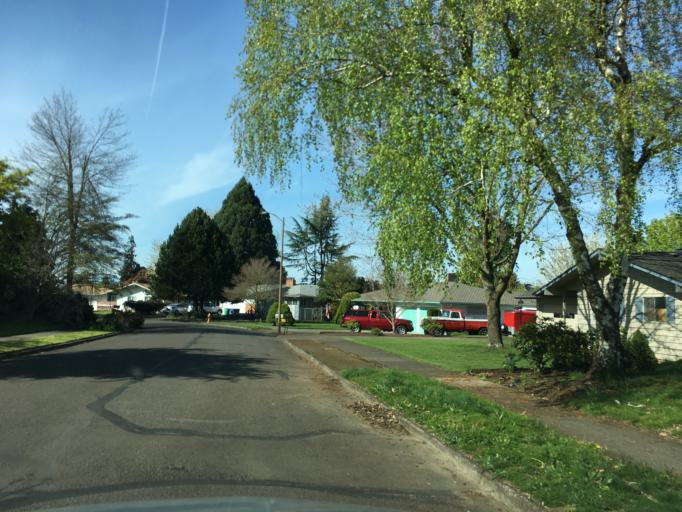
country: US
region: Oregon
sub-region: Multnomah County
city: Lents
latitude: 45.5411
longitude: -122.5149
